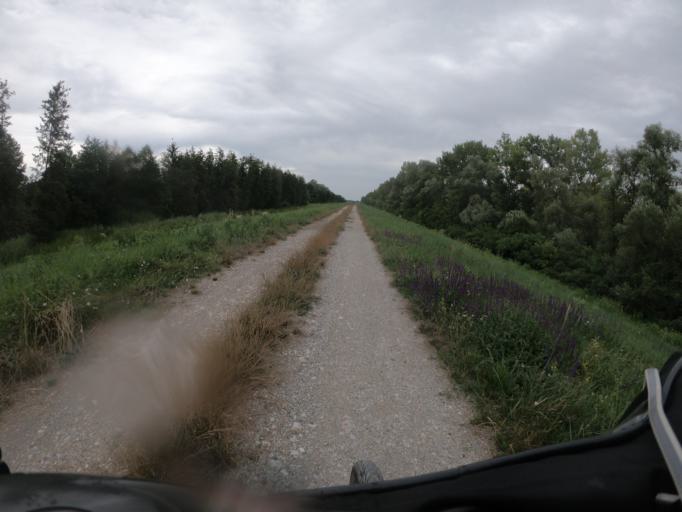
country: HU
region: Jasz-Nagykun-Szolnok
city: Tiszafured
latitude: 47.6789
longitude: 20.7673
